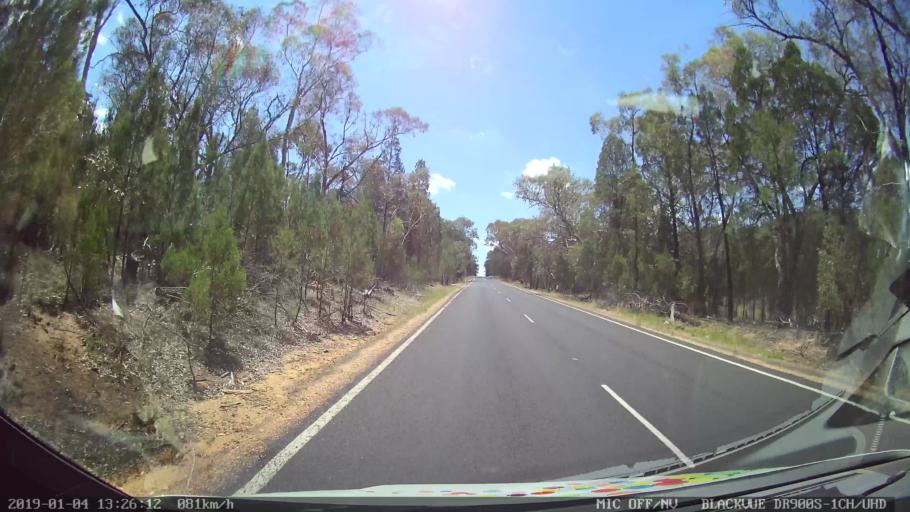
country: AU
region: New South Wales
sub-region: Parkes
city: Peak Hill
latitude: -32.6836
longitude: 148.5564
